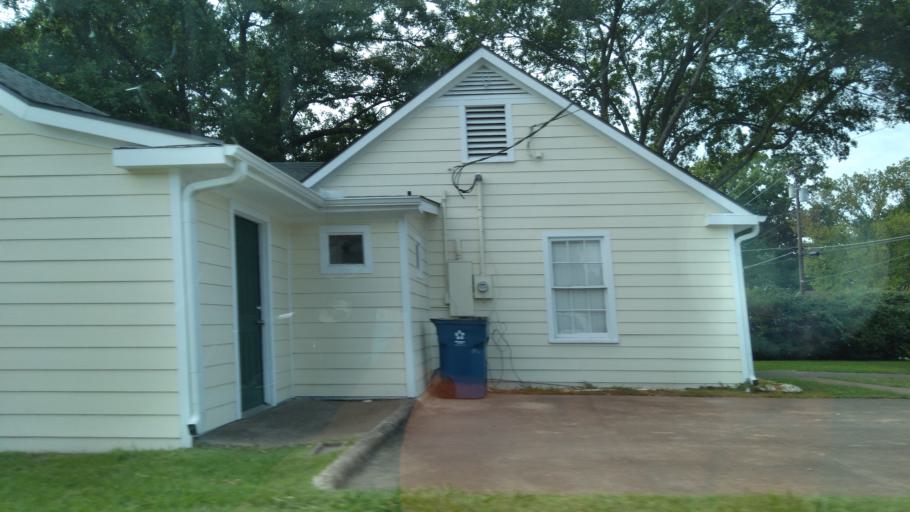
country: US
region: Texas
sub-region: Navarro County
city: Corsicana
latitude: 32.0813
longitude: -96.4853
